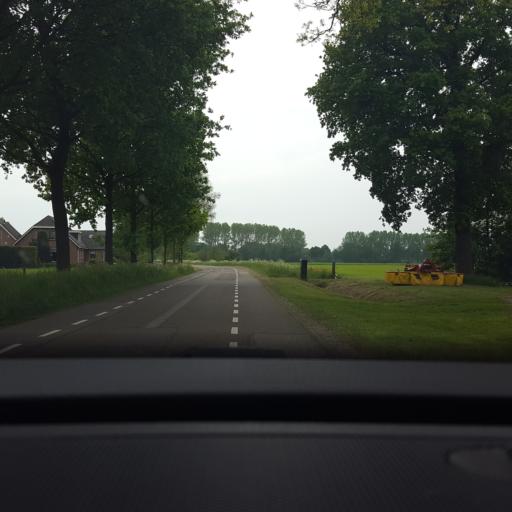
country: NL
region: Gelderland
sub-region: Gemeente Lochem
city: Barchem
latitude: 52.0502
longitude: 6.4497
